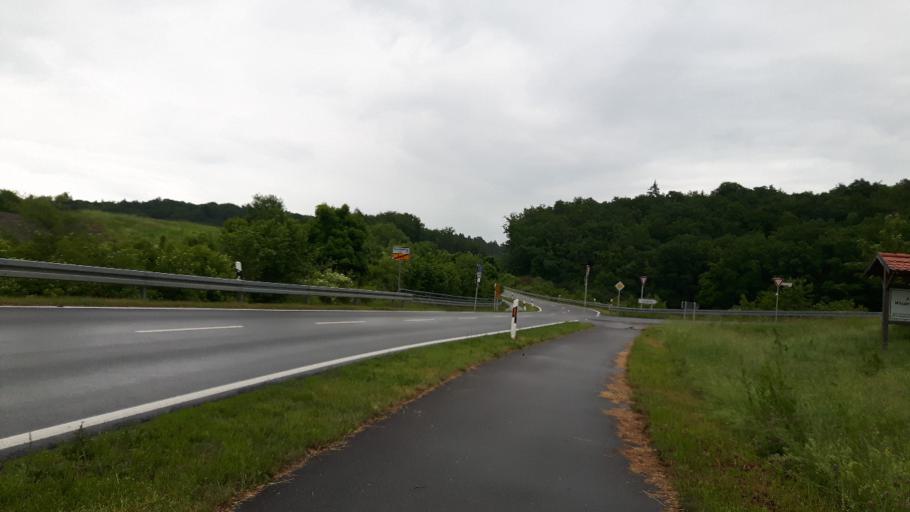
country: DE
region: Bavaria
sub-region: Regierungsbezirk Unterfranken
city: Uchtelhausen
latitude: 50.0985
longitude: 10.2485
